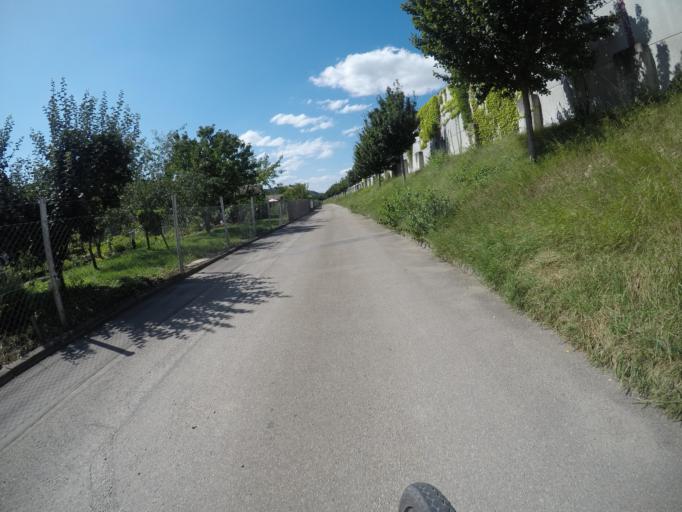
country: DE
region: Baden-Wuerttemberg
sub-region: Regierungsbezirk Stuttgart
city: Denkendorf
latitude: 48.7215
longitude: 9.3378
